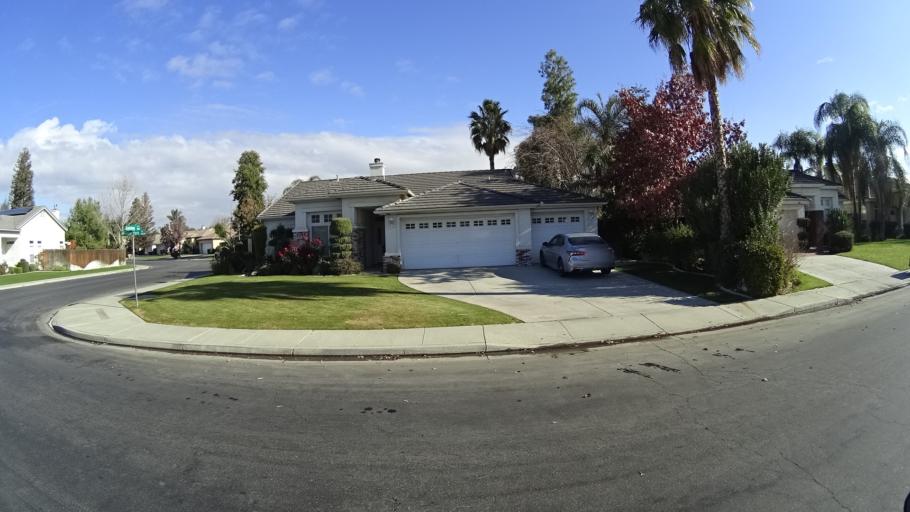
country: US
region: California
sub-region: Kern County
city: Greenacres
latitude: 35.3494
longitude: -119.1158
